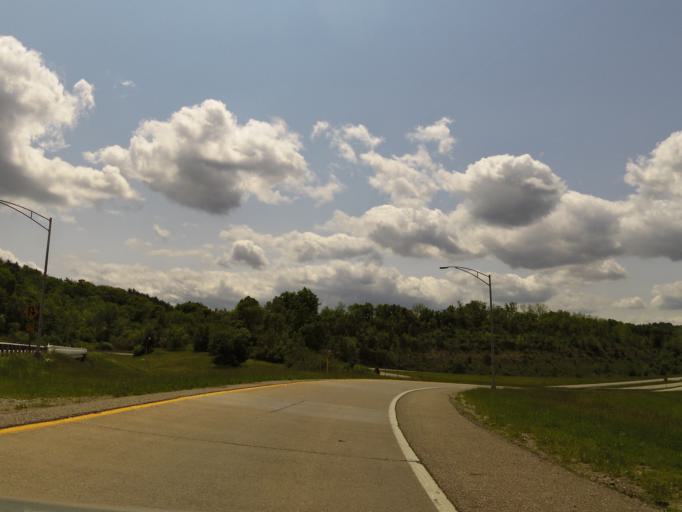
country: US
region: Ohio
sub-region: Athens County
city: Athens
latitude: 39.3148
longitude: -82.0987
